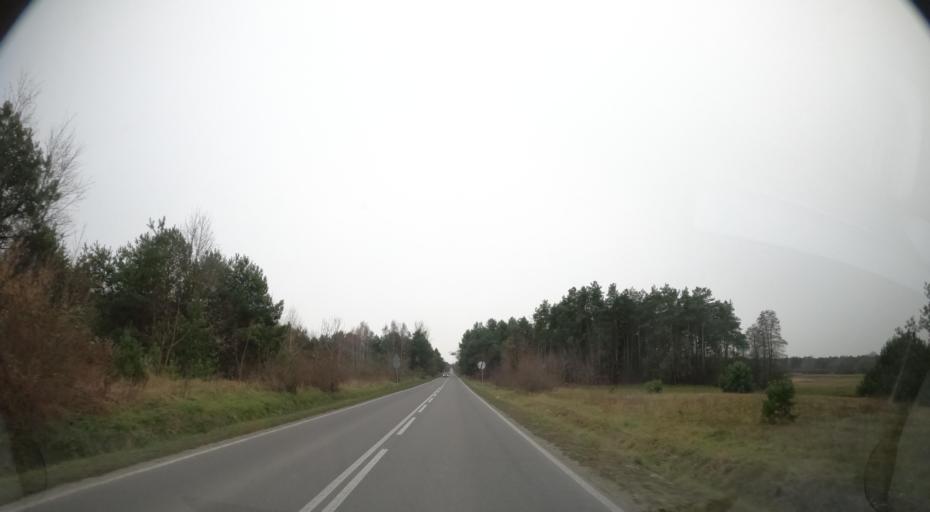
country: PL
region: Masovian Voivodeship
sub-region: Powiat radomski
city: Jastrzebia
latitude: 51.4681
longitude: 21.2000
